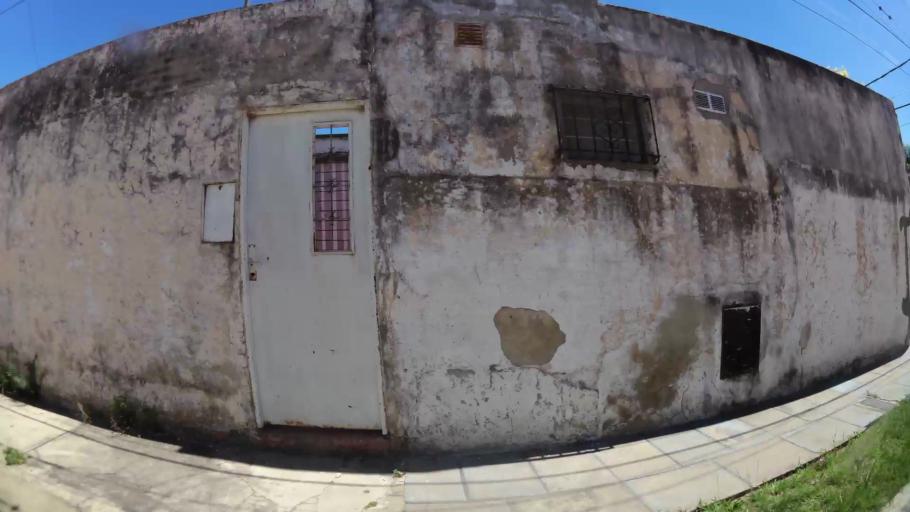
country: AR
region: Santa Fe
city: Santa Fe de la Vera Cruz
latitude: -31.6567
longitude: -60.7254
